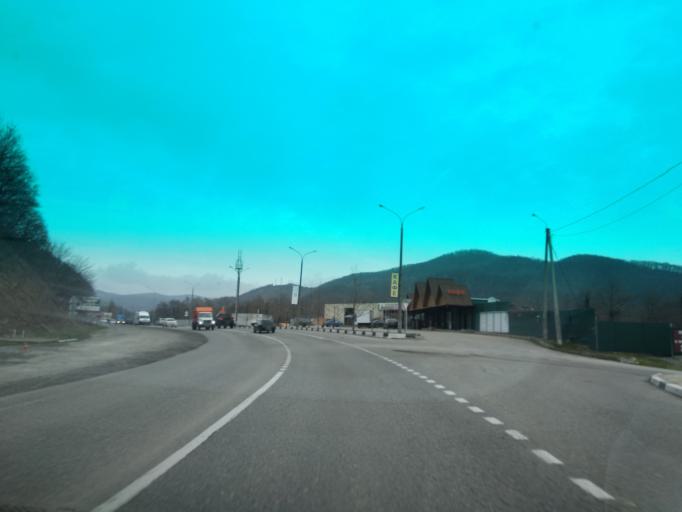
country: RU
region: Krasnodarskiy
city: Ol'ginka
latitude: 44.2133
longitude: 38.8946
